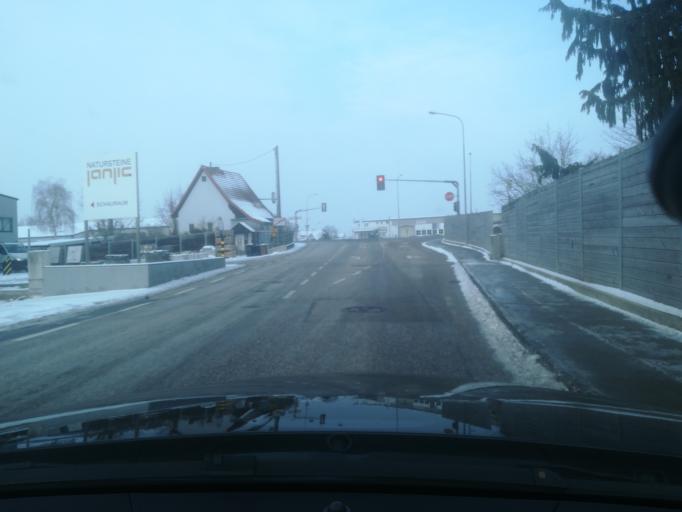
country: AT
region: Upper Austria
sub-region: Wels-Land
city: Marchtrenk
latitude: 48.1962
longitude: 14.1407
